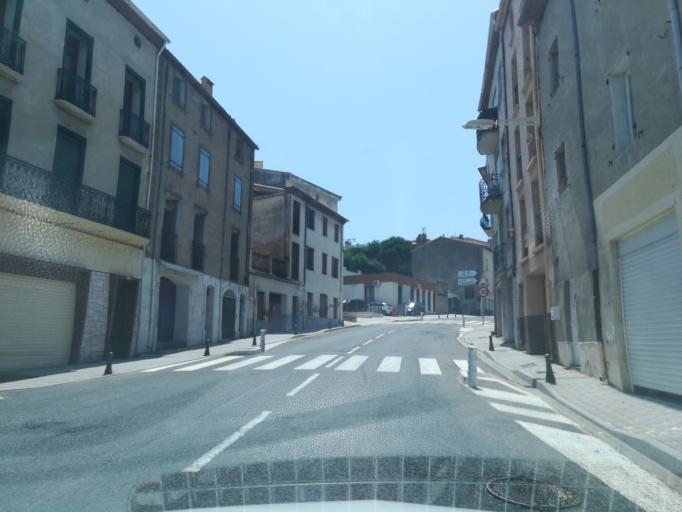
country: ES
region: Catalonia
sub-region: Provincia de Girona
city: la Jonquera
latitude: 42.4660
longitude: 2.8630
